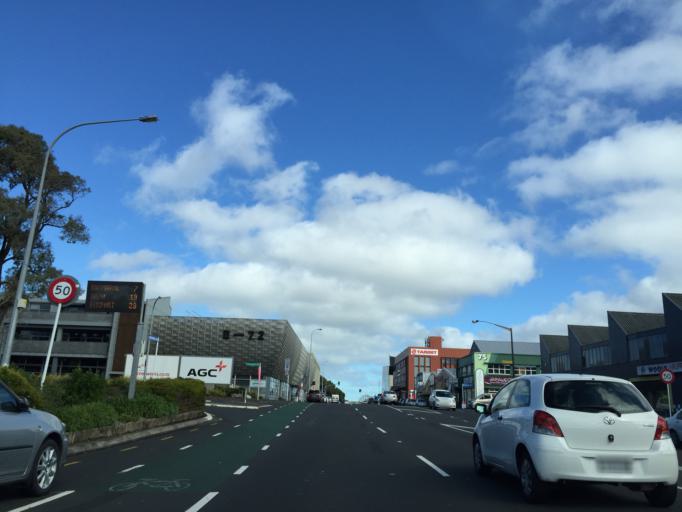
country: NZ
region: Auckland
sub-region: Auckland
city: Auckland
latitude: -36.8702
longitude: 174.7530
